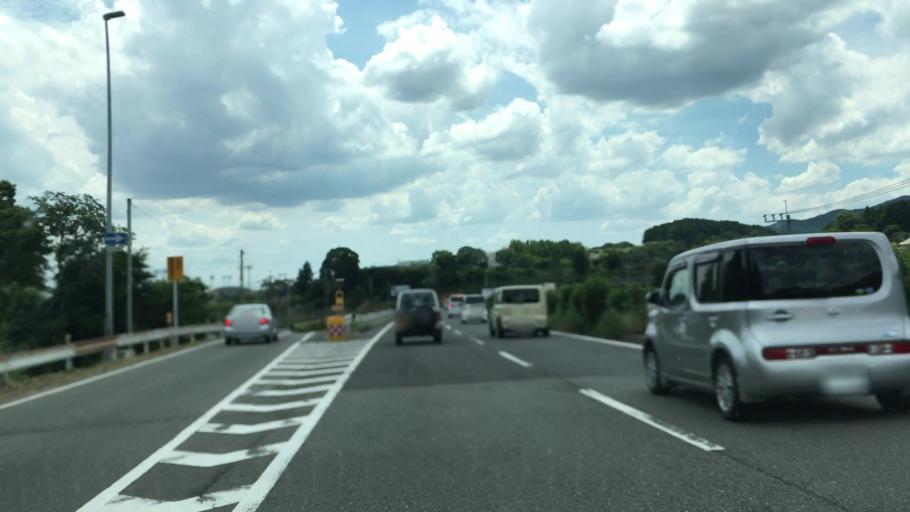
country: JP
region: Fukuoka
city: Chikushino-shi
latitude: 33.4351
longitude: 130.5246
